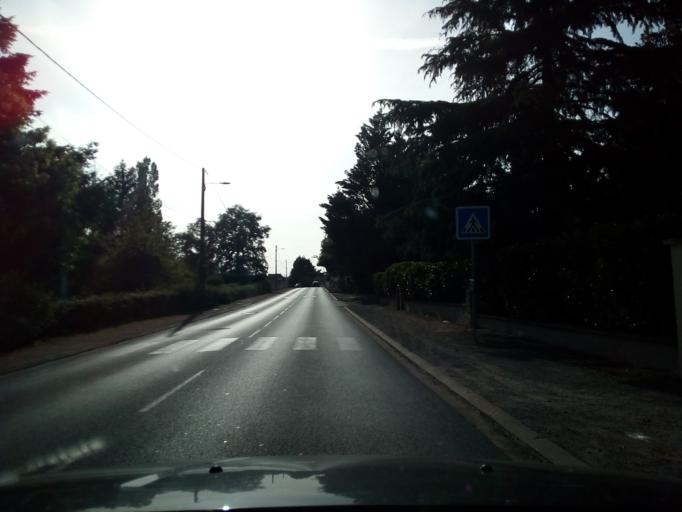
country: FR
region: Auvergne
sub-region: Departement de l'Allier
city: Domerat
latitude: 46.3596
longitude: 2.5456
